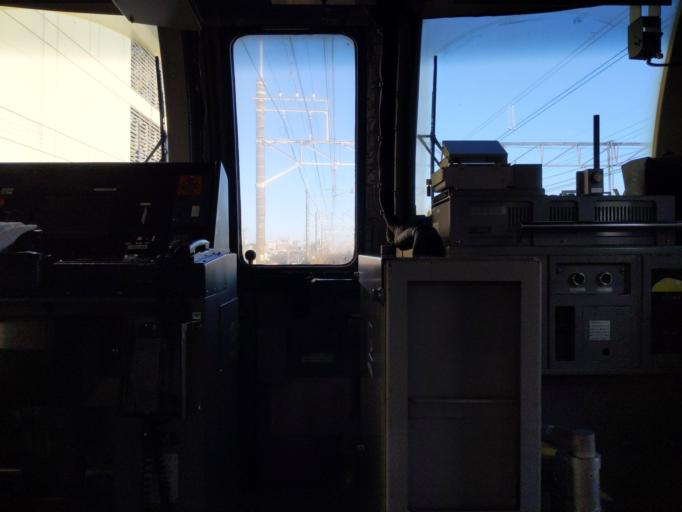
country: JP
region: Chiba
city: Funabashi
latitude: 35.7141
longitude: 139.9440
